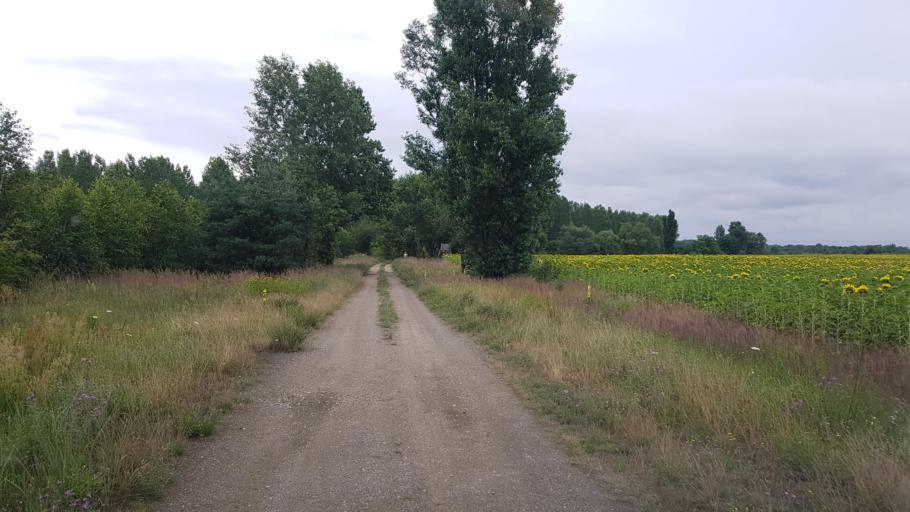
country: DE
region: Brandenburg
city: Spremberg
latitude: 51.5970
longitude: 14.3219
